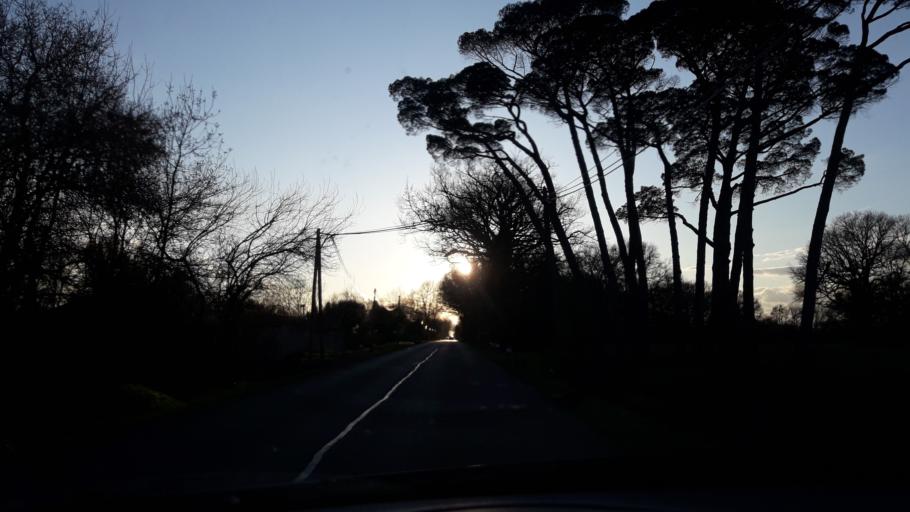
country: FR
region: Midi-Pyrenees
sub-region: Departement du Gers
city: Pujaudran
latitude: 43.6332
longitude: 1.1392
